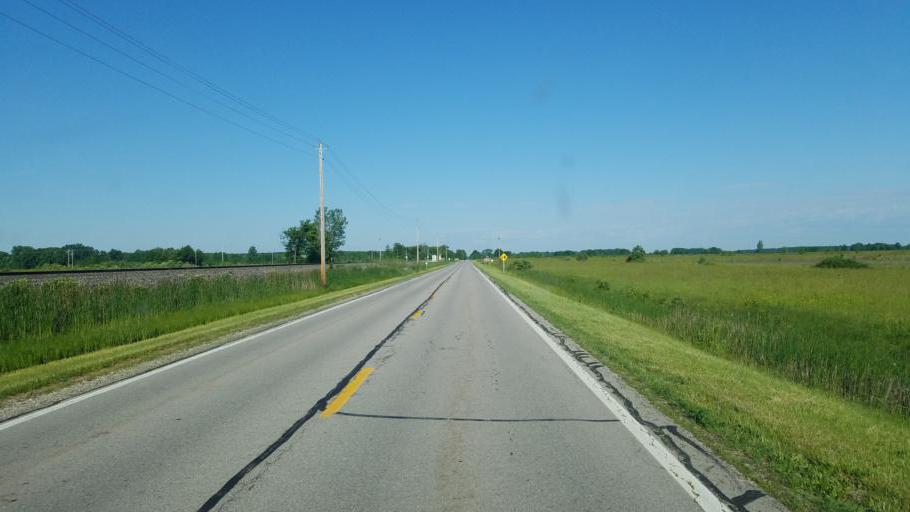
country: US
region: Ohio
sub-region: Marion County
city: Marion
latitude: 40.5862
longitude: -83.2516
